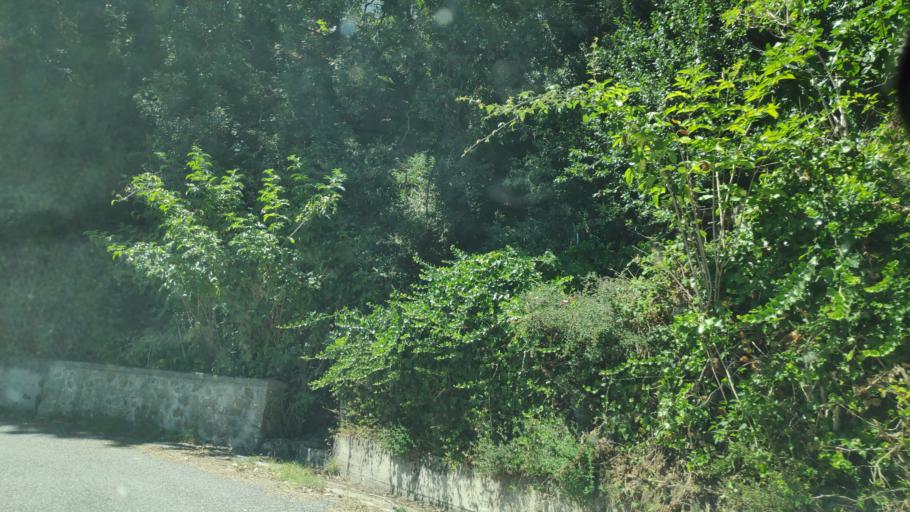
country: IT
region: Calabria
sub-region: Provincia di Catanzaro
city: Gasperina
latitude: 38.7419
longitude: 16.5074
